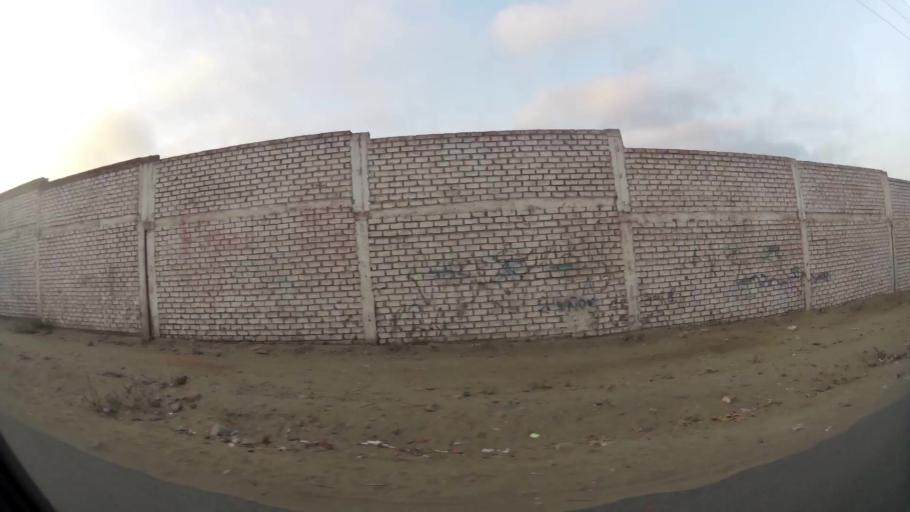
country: PE
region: La Libertad
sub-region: Provincia de Trujillo
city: El Porvenir
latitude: -8.0724
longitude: -79.0031
